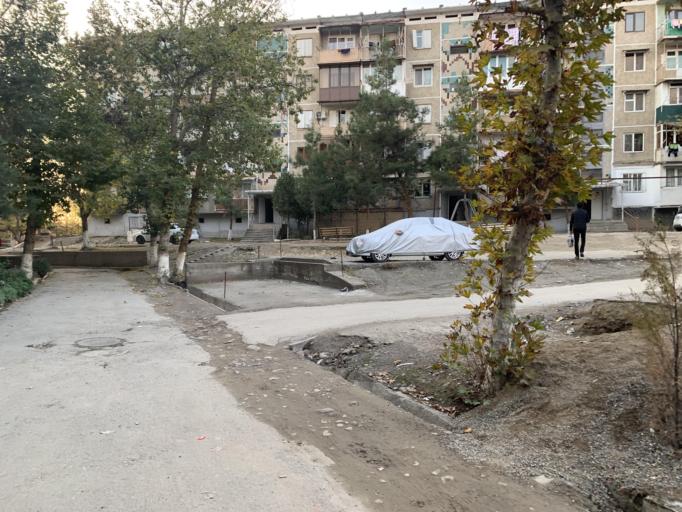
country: UZ
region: Namangan
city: Namangan Shahri
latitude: 41.0053
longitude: 71.5983
